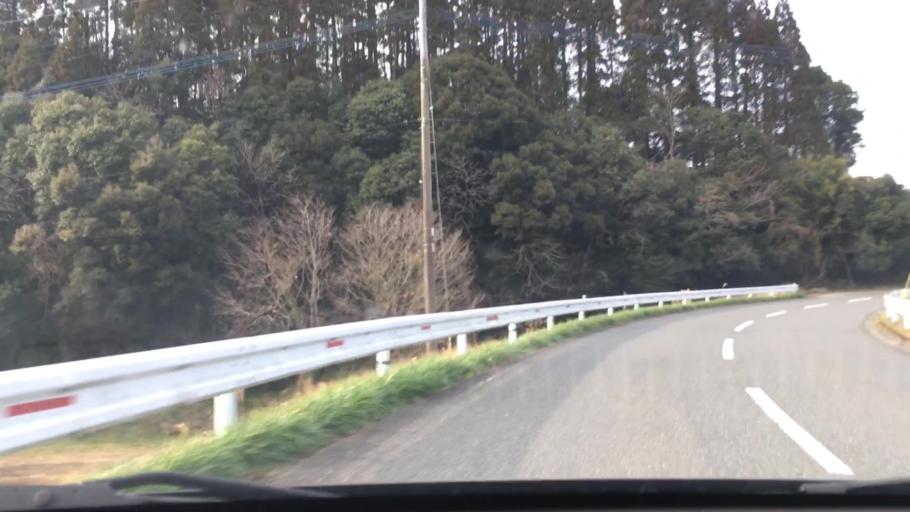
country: JP
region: Miyazaki
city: Nichinan
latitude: 31.6169
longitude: 131.3356
